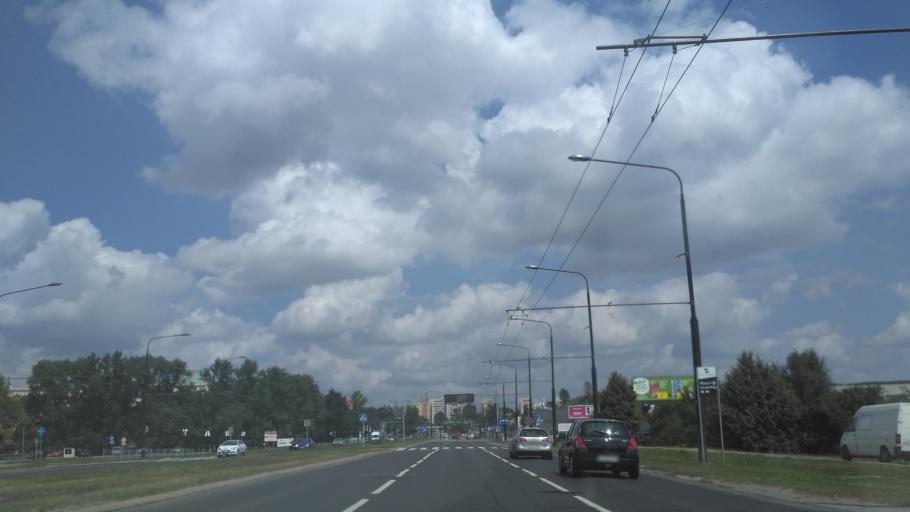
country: PL
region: Lublin Voivodeship
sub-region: Powiat lubelski
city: Lublin
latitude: 51.2463
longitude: 22.5740
